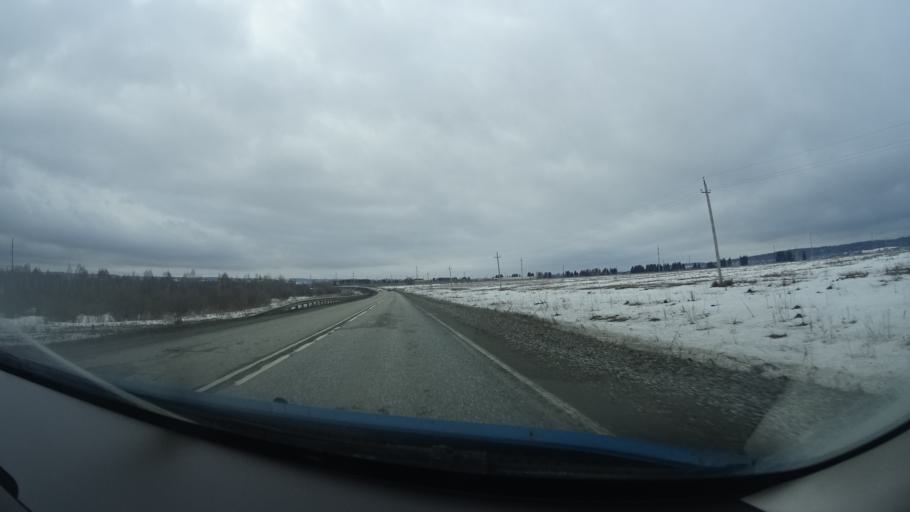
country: RU
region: Perm
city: Barda
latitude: 56.9538
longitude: 55.5823
